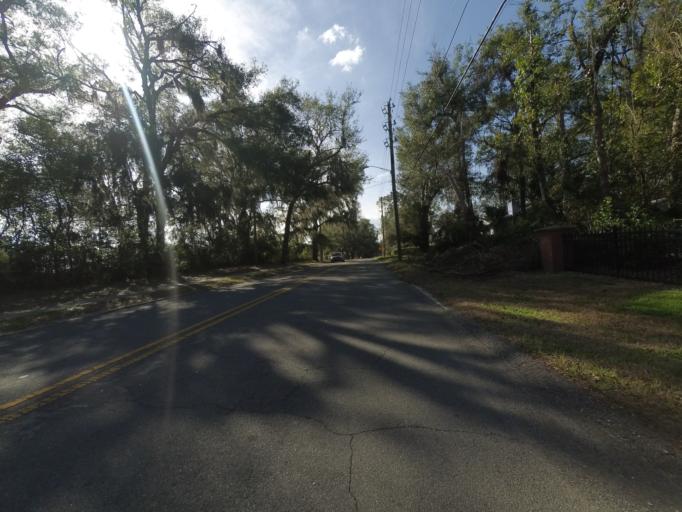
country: US
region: Florida
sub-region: Lake County
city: Mount Dora
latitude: 28.8060
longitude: -81.6496
